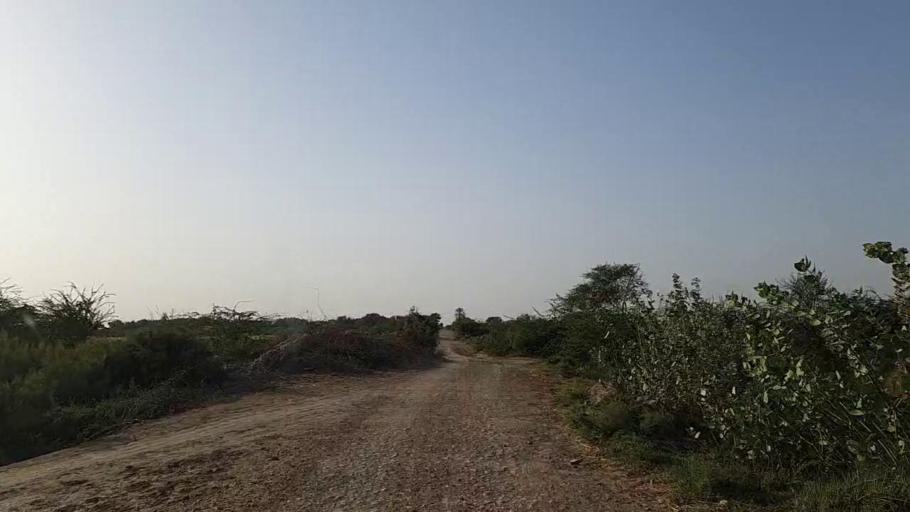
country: PK
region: Sindh
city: Jati
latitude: 24.3432
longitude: 68.1457
